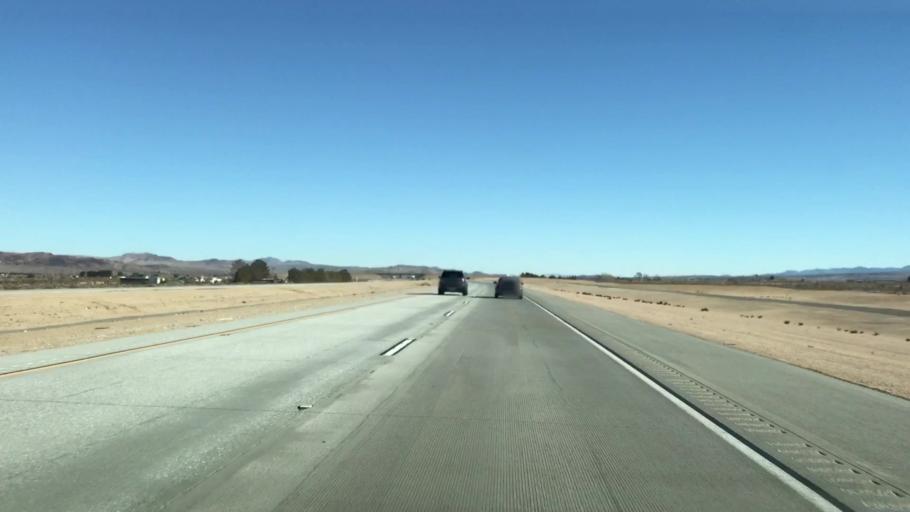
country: US
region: California
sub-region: San Bernardino County
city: Lenwood
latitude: 34.9135
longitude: -117.2047
